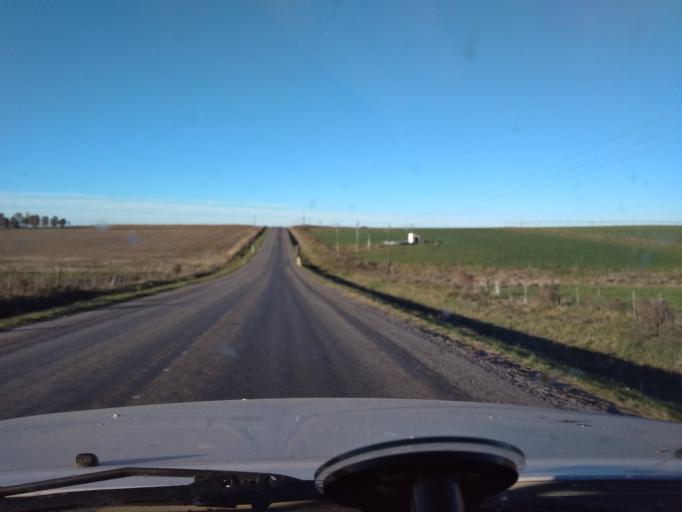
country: UY
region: Florida
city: Casupa
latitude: -34.0335
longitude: -55.8802
